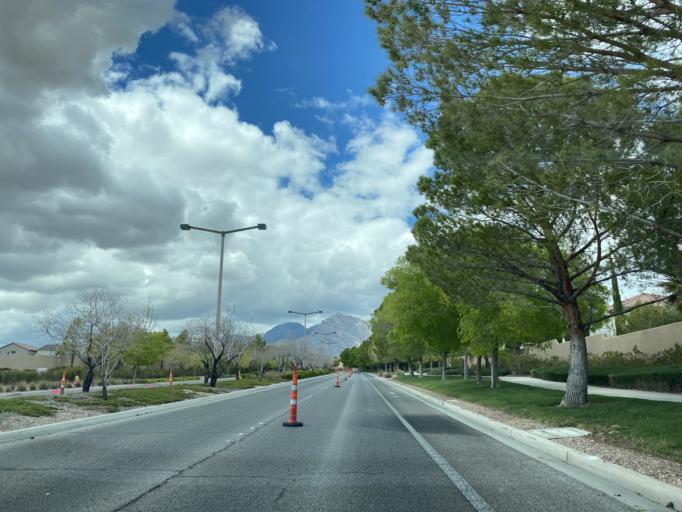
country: US
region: Nevada
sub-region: Clark County
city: Summerlin South
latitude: 36.1718
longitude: -115.3451
